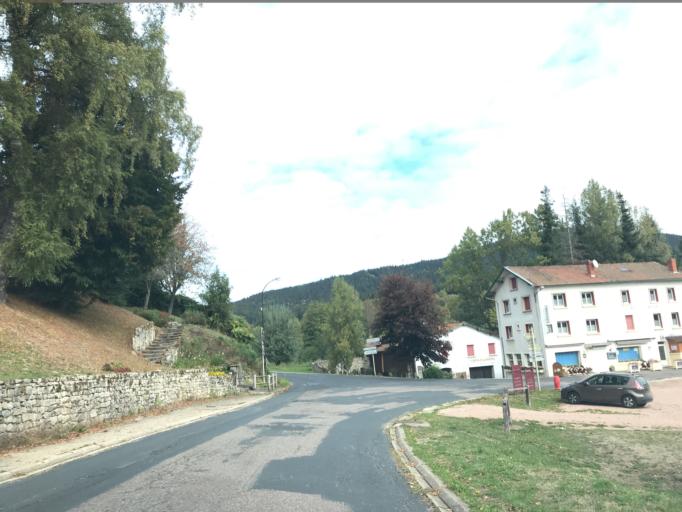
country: FR
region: Auvergne
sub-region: Departement du Puy-de-Dome
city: Celles-sur-Durolle
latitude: 45.7858
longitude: 3.6736
